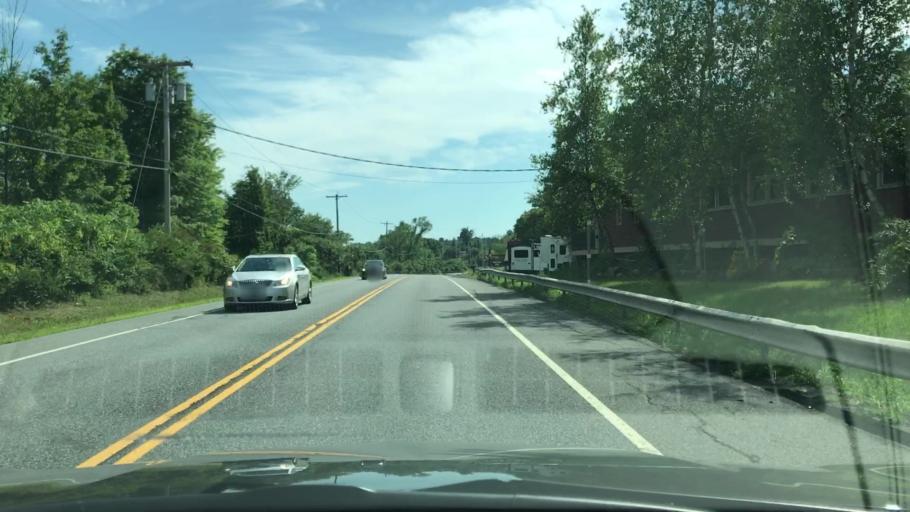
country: US
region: Vermont
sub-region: Rutland County
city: Fair Haven
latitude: 43.5752
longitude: -73.3113
